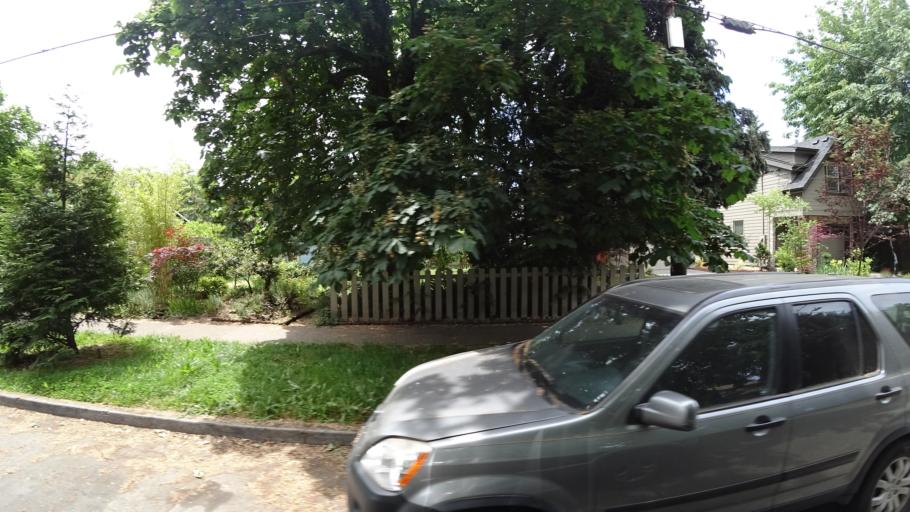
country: US
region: Oregon
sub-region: Washington County
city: West Haven
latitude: 45.5953
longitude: -122.7539
